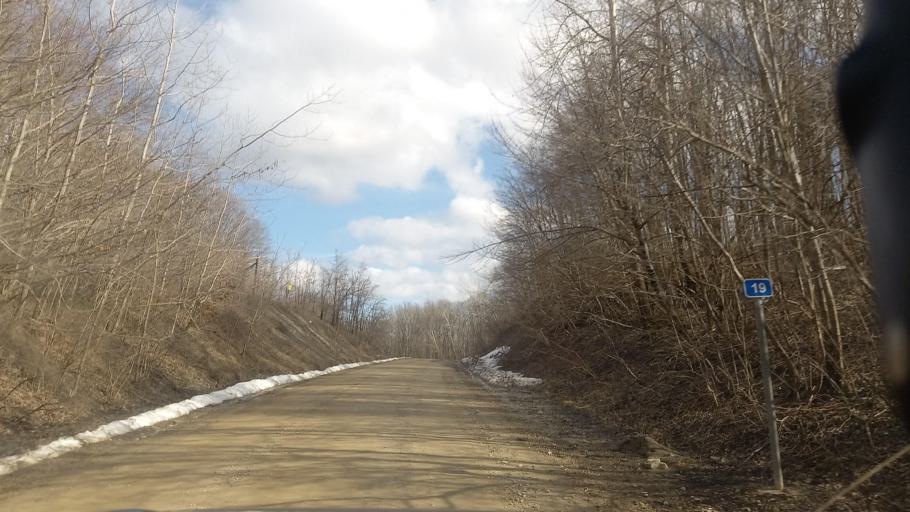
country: RU
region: Krasnodarskiy
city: Smolenskaya
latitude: 44.6061
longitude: 38.7681
